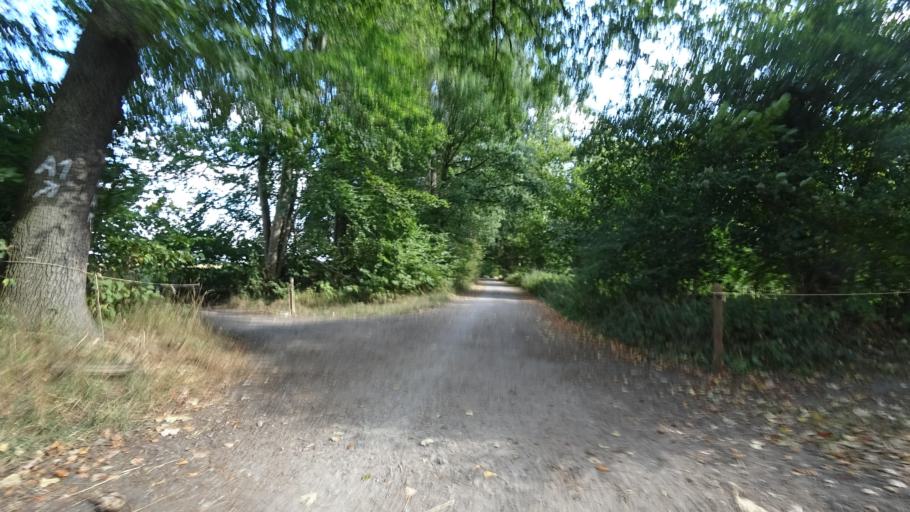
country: DE
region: North Rhine-Westphalia
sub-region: Regierungsbezirk Detmold
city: Rheda-Wiedenbruck
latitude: 51.8318
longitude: 8.2744
